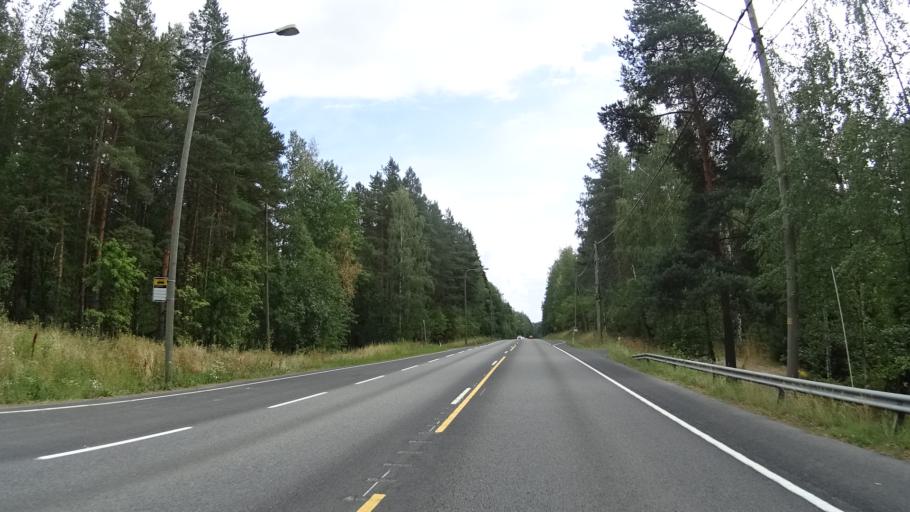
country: FI
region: Pirkanmaa
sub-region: Tampere
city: Kangasala
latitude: 61.4291
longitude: 24.1311
